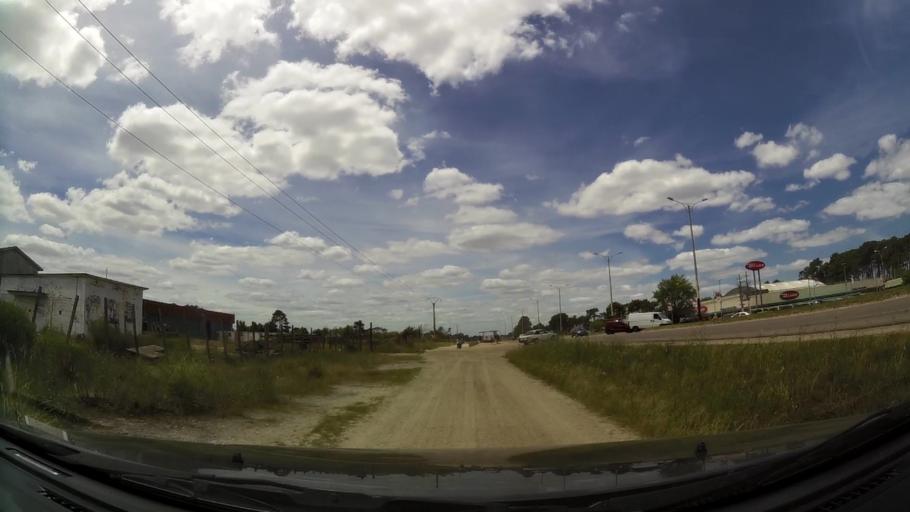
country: UY
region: Canelones
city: Pando
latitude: -34.8054
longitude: -55.9290
